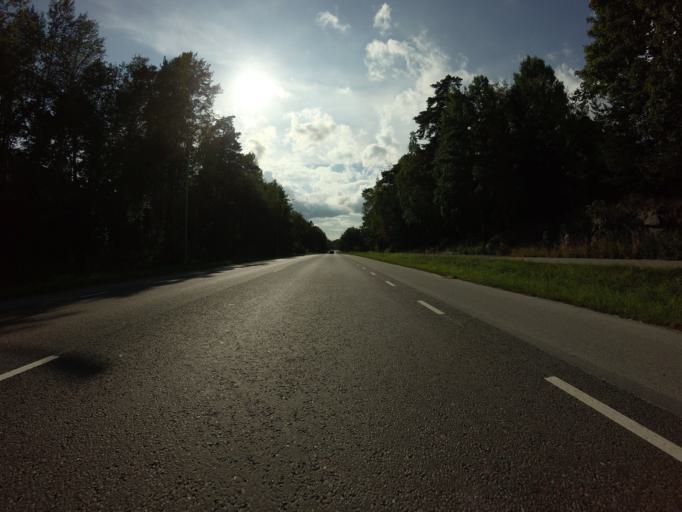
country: SE
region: Stockholm
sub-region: Lidingo
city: Lidingoe
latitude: 59.3709
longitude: 18.1379
